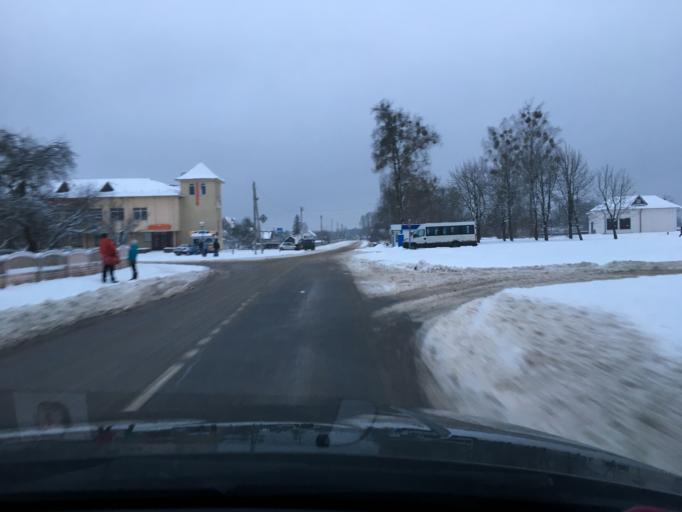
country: LT
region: Alytaus apskritis
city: Druskininkai
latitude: 53.8859
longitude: 24.1357
